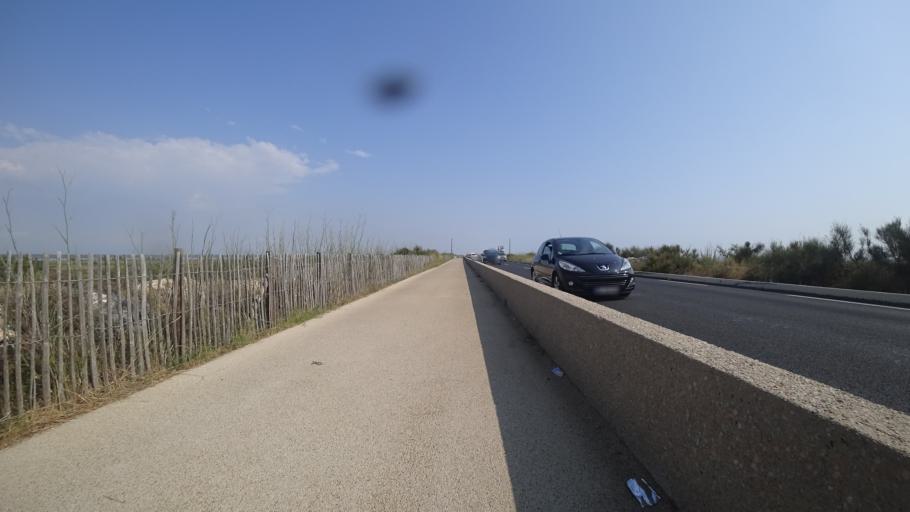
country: FR
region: Languedoc-Roussillon
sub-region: Departement des Pyrenees-Orientales
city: Saint-Cyprien-Plage
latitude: 42.6557
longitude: 3.0328
